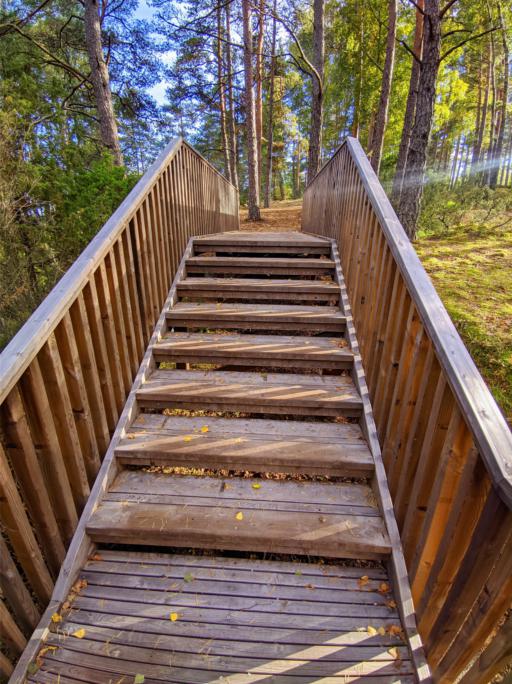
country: SE
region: Vaestra Goetaland
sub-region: Tanums Kommun
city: Tanumshede
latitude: 58.7007
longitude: 11.3367
